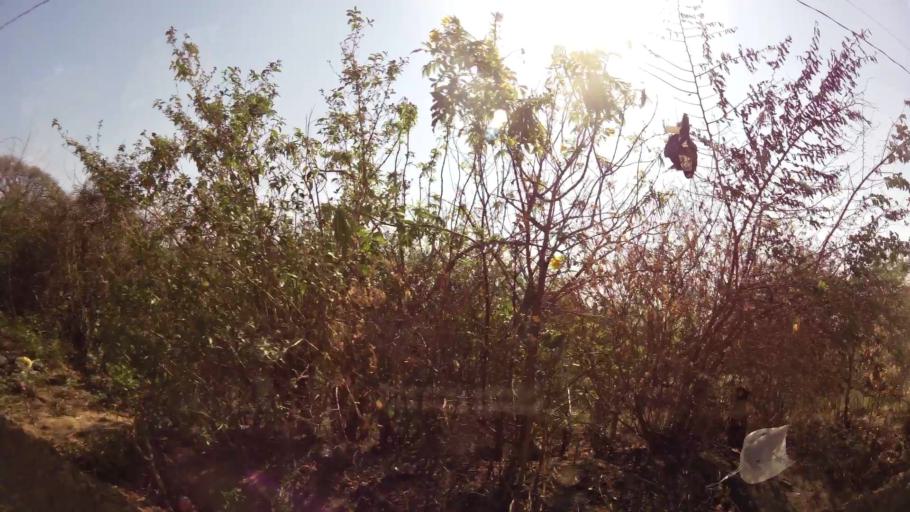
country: BO
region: Santa Cruz
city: Cotoca
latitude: -17.7341
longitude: -63.0741
